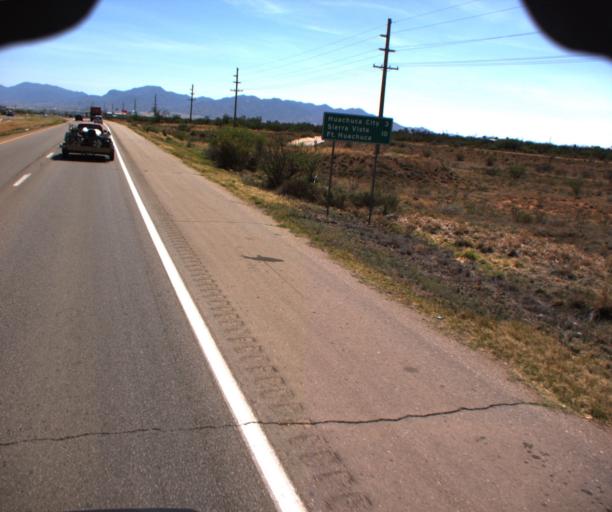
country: US
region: Arizona
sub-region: Cochise County
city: Huachuca City
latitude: 31.6917
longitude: -110.3504
